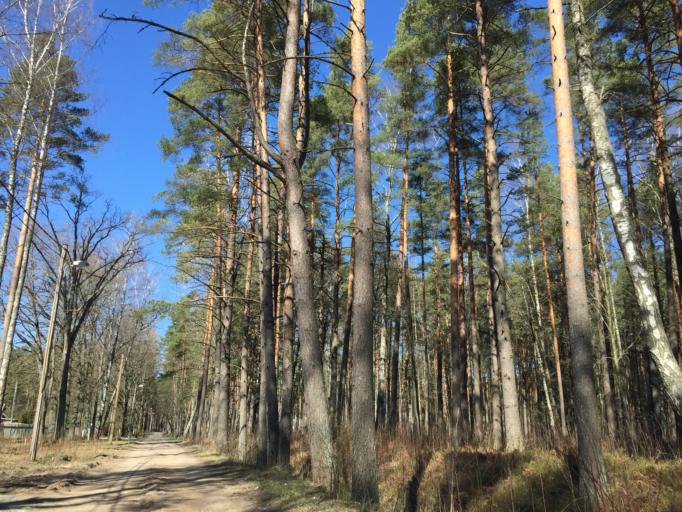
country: LV
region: Jurmala
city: Jurmala
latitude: 56.9468
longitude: 23.6777
